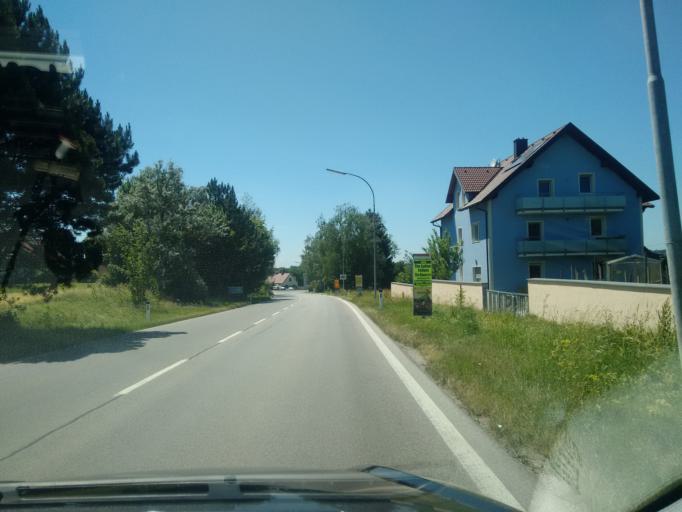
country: AT
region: Lower Austria
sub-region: Politischer Bezirk Sankt Polten
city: Herzogenburg
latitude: 48.2420
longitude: 15.7070
